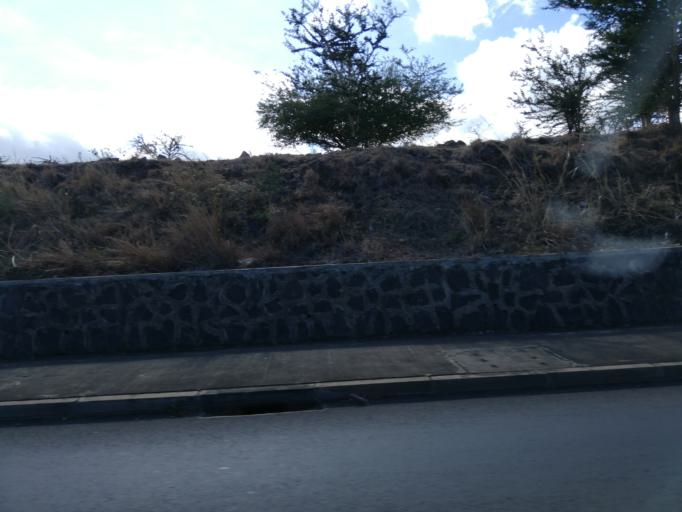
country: MU
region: Moka
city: Pailles
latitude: -20.1801
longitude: 57.4740
